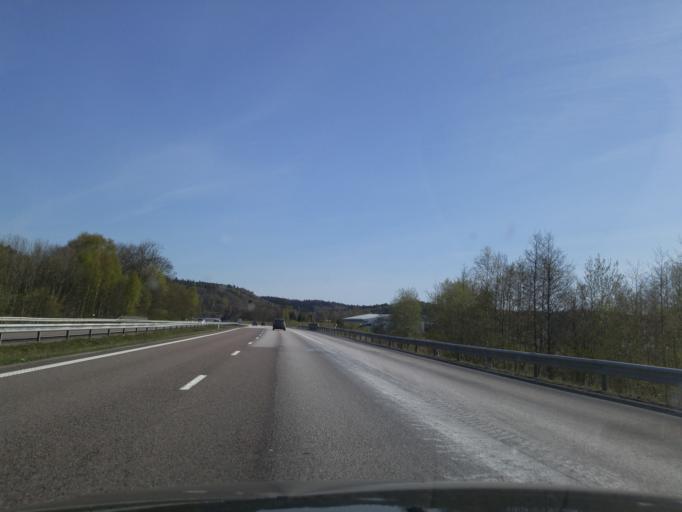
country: SE
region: Vaestra Goetaland
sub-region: Stenungsunds Kommun
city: Stenungsund
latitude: 58.0600
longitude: 11.8832
